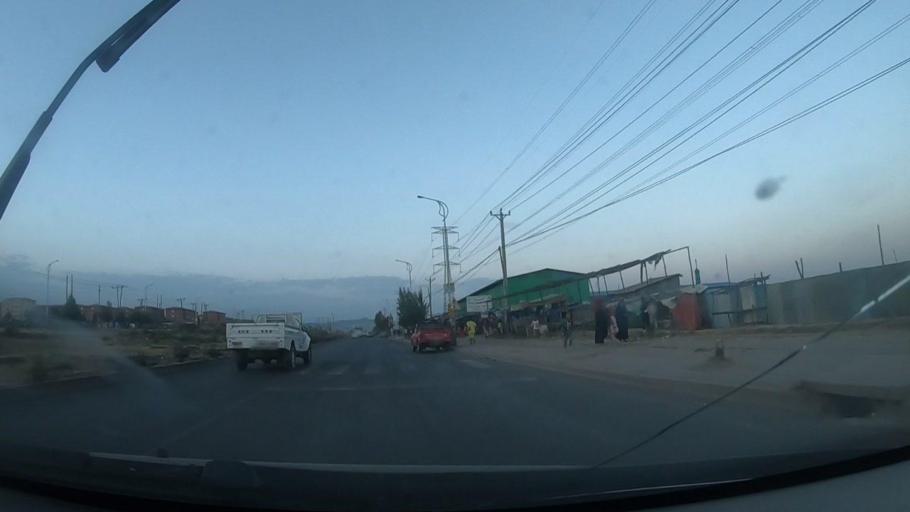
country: ET
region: Adis Abeba
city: Addis Ababa
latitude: 9.0443
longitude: 38.8779
